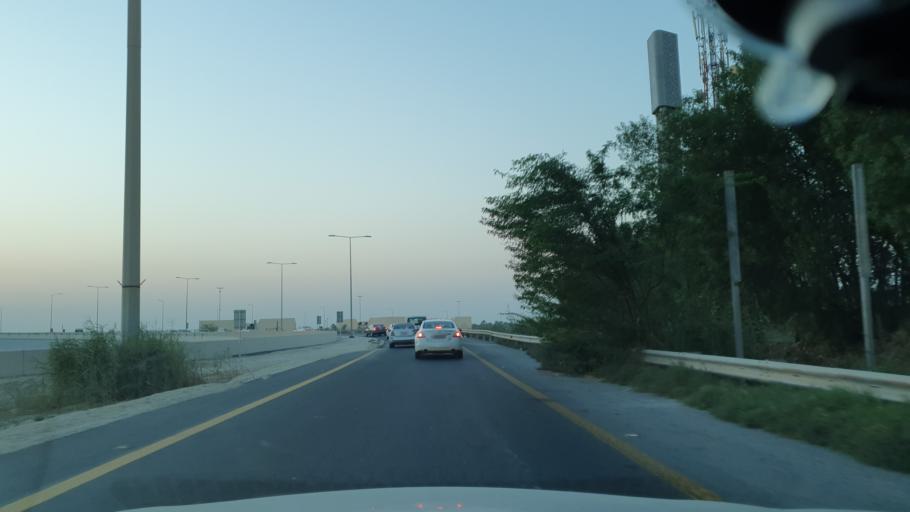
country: BH
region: Central Governorate
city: Madinat Hamad
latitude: 26.1739
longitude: 50.4677
